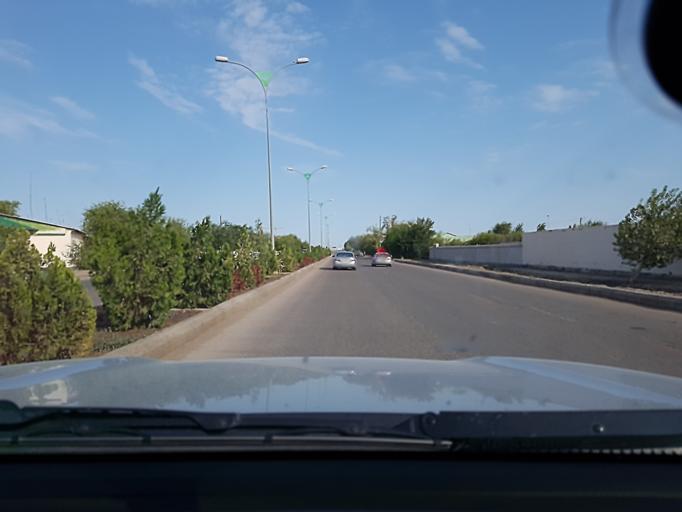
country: TM
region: Dasoguz
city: Koeneuergench
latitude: 42.3198
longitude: 59.1609
